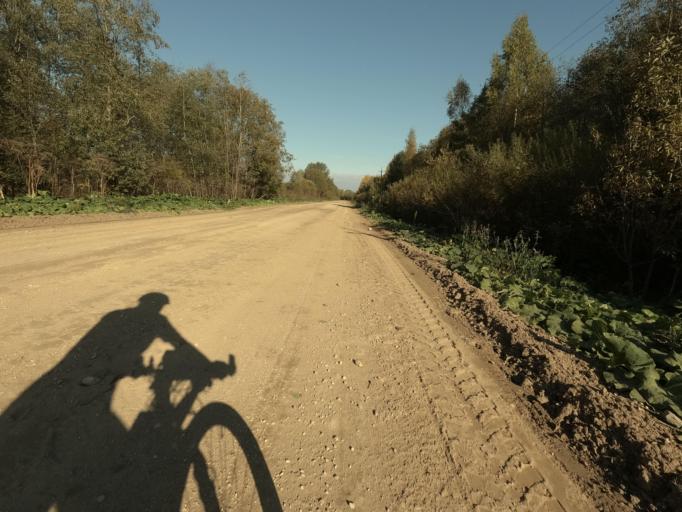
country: RU
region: Novgorod
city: Batetskiy
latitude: 58.8760
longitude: 30.7257
